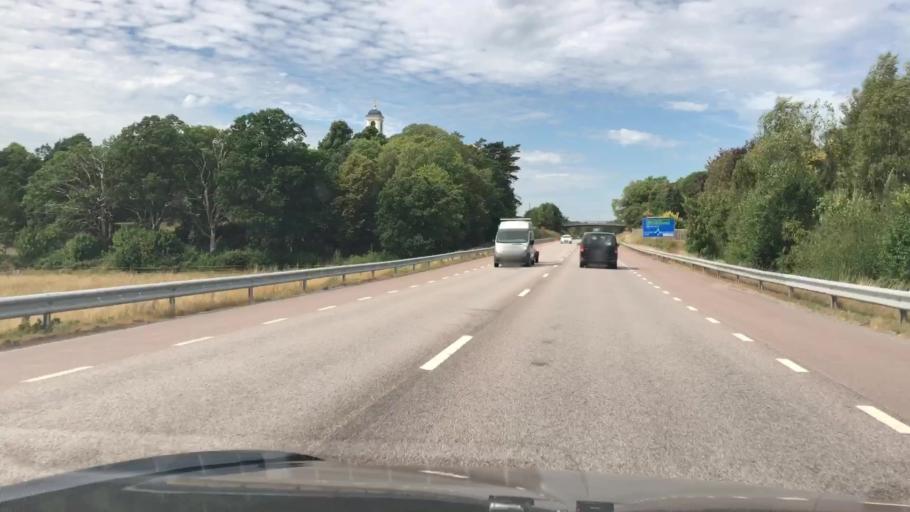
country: SE
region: Blekinge
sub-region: Karlskrona Kommun
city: Rodeby
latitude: 56.1970
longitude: 15.6923
